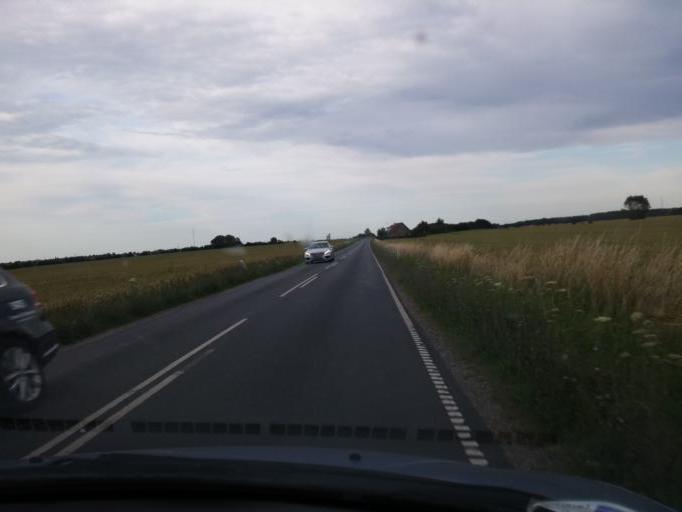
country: DK
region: South Denmark
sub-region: Kerteminde Kommune
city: Kerteminde
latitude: 55.4351
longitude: 10.6322
